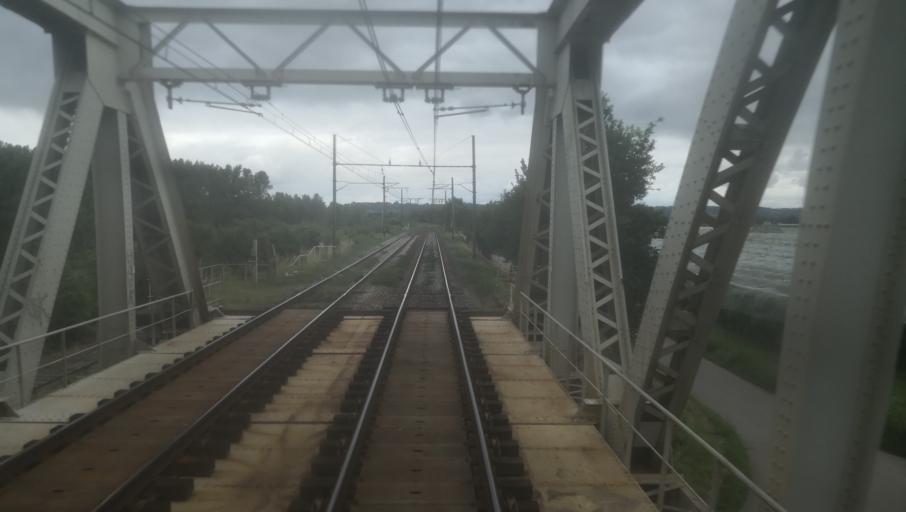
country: FR
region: Midi-Pyrenees
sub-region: Departement du Tarn-et-Garonne
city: Moissac
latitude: 44.0926
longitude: 1.1054
